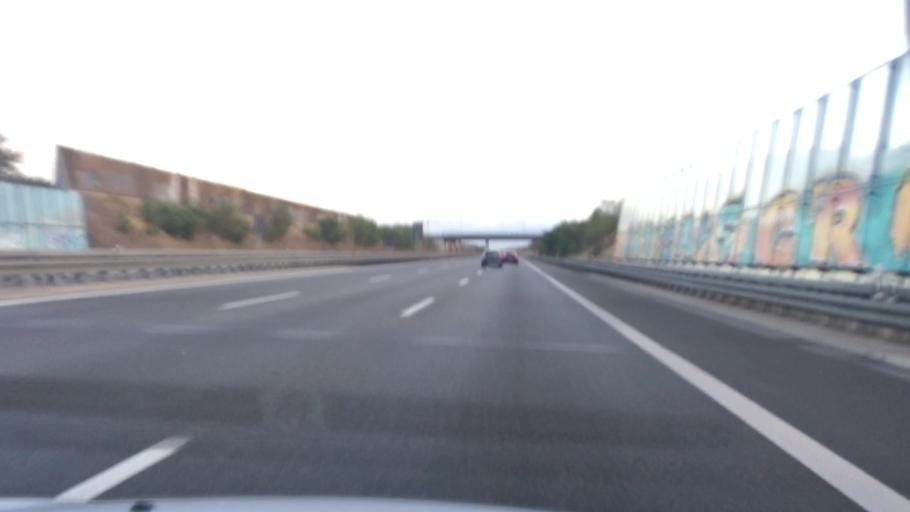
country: DE
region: Saxony
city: Taucha
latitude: 51.3860
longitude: 12.4458
